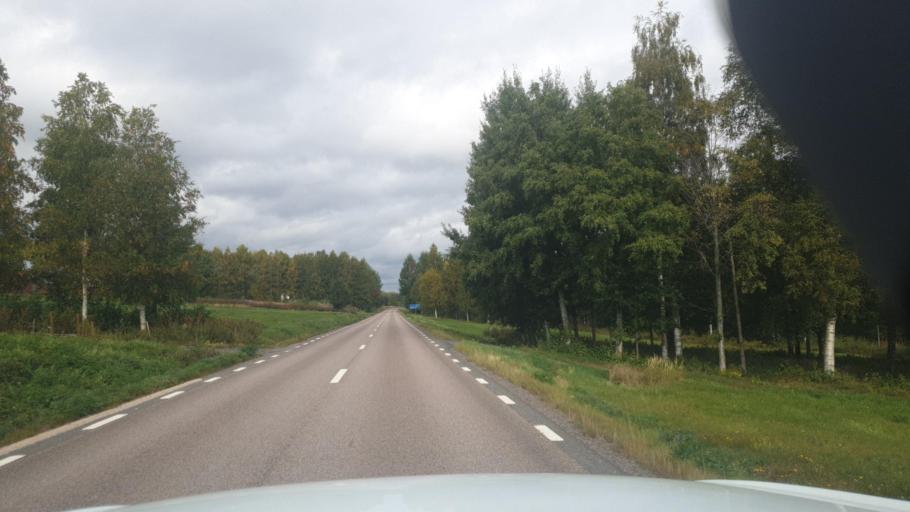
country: SE
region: Vaermland
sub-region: Torsby Kommun
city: Torsby
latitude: 59.9214
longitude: 12.8977
